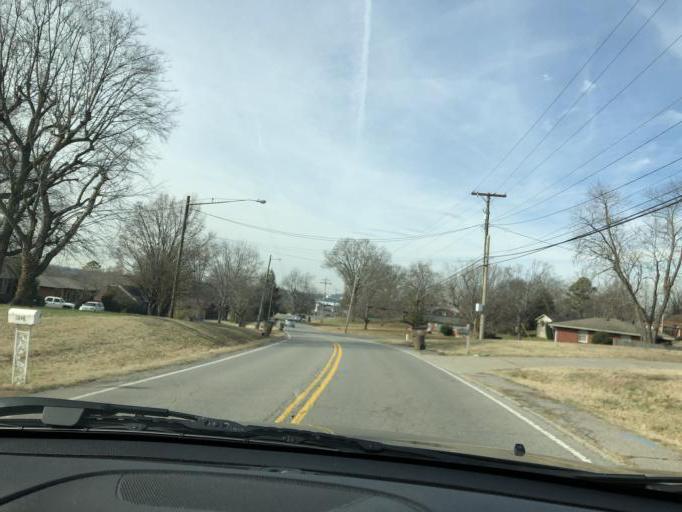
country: US
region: Tennessee
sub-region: Davidson County
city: Lakewood
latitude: 36.2087
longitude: -86.6824
